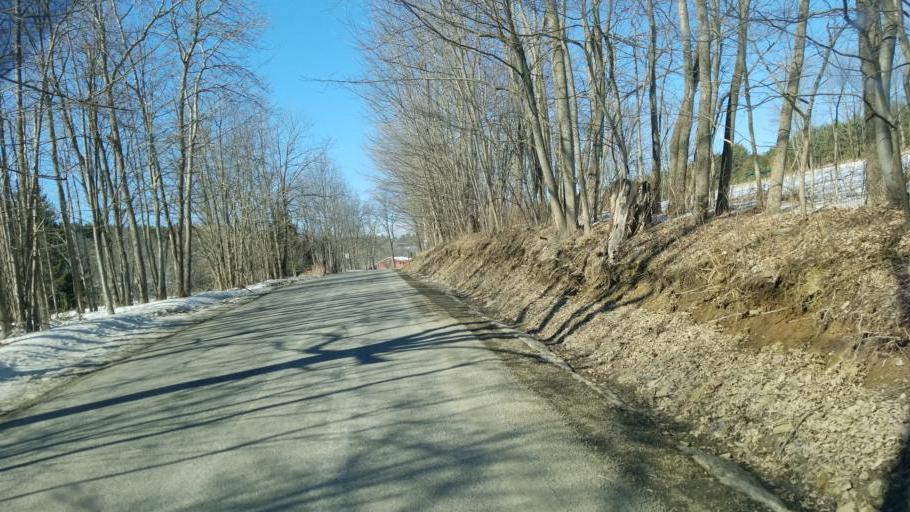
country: US
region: Pennsylvania
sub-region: Tioga County
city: Westfield
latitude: 41.9870
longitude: -77.6726
